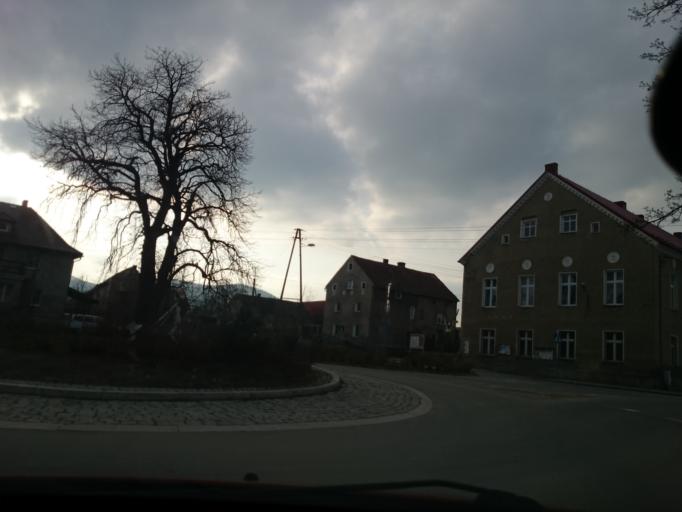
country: PL
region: Lower Silesian Voivodeship
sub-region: Powiat zabkowicki
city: Bardo
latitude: 50.5393
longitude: 16.7315
